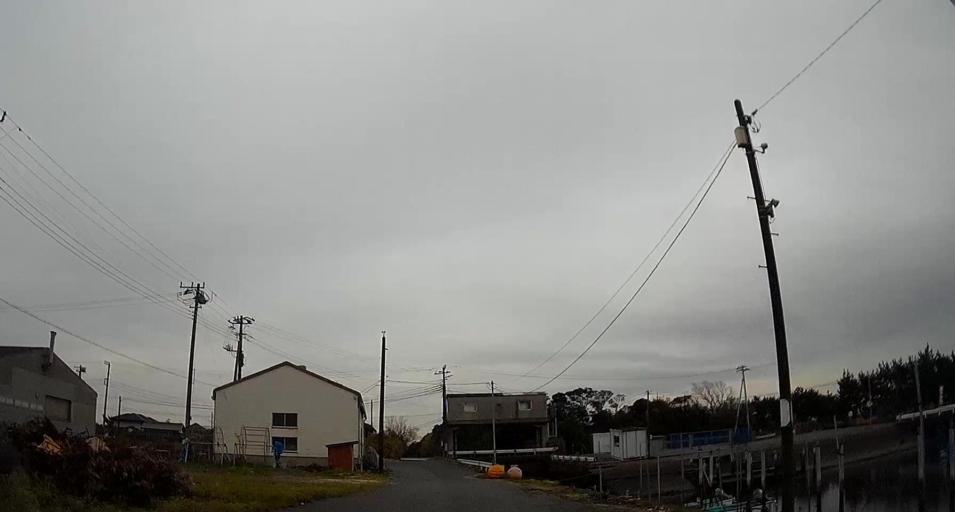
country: JP
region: Chiba
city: Kisarazu
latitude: 35.4053
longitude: 139.9033
